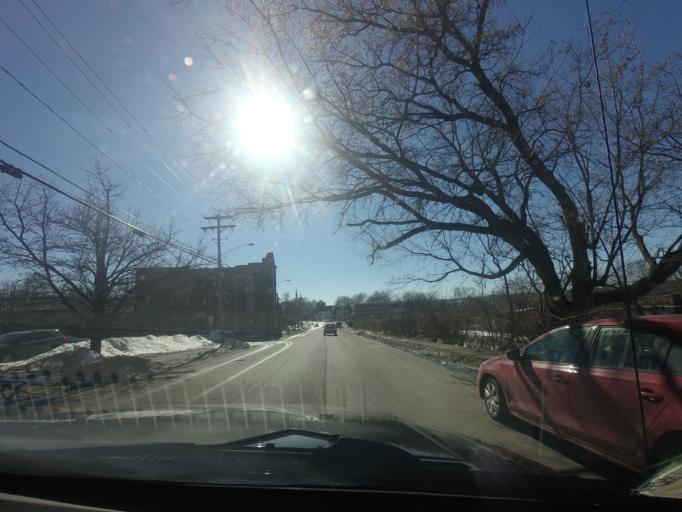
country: US
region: New York
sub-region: Albany County
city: Green Island
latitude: 42.7418
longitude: -73.6785
